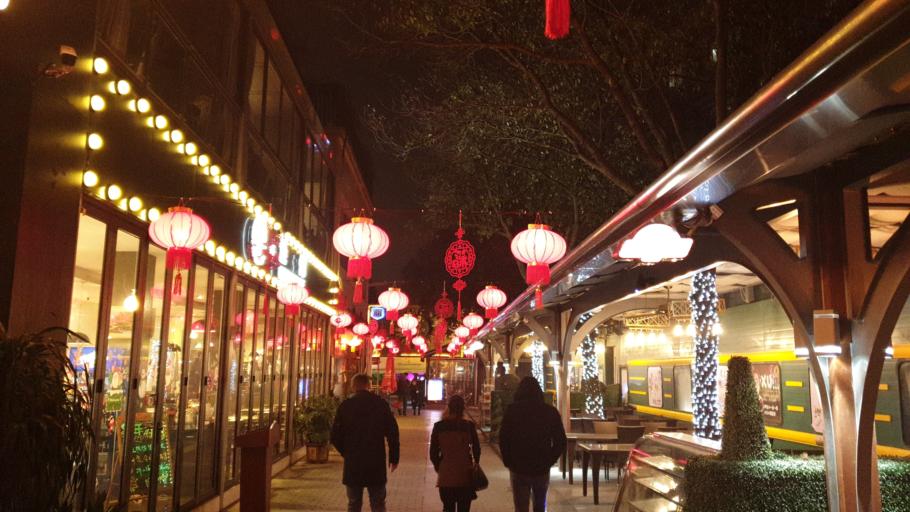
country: CN
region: Shanghai Shi
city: Changning
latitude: 31.1930
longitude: 121.3816
